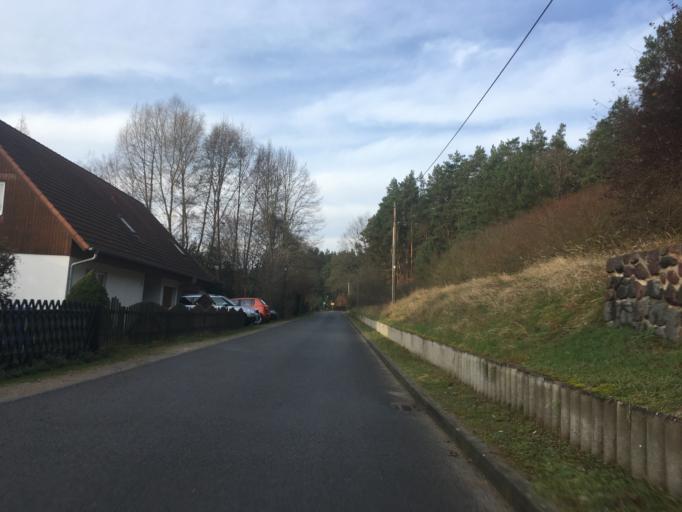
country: DE
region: Brandenburg
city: Niederfinow
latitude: 52.8439
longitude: 13.9054
